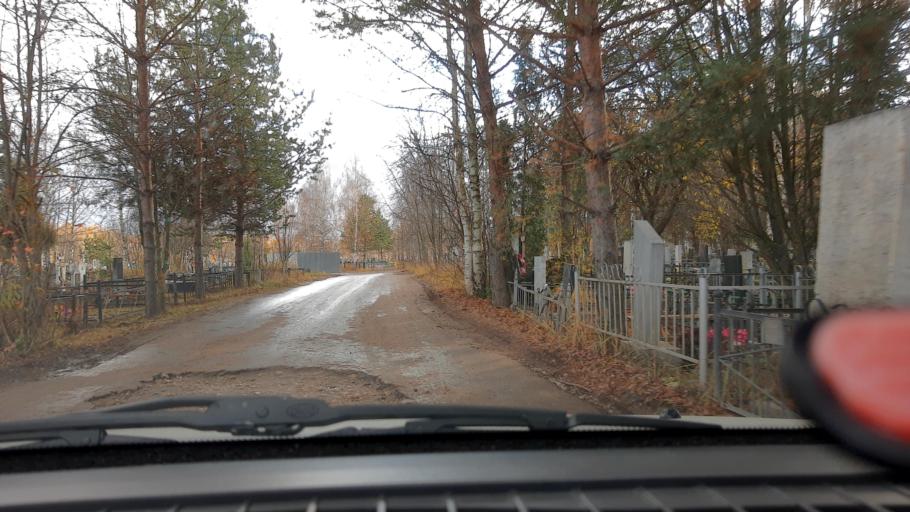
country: RU
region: Nizjnij Novgorod
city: Gorbatovka
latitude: 56.3594
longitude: 43.7734
